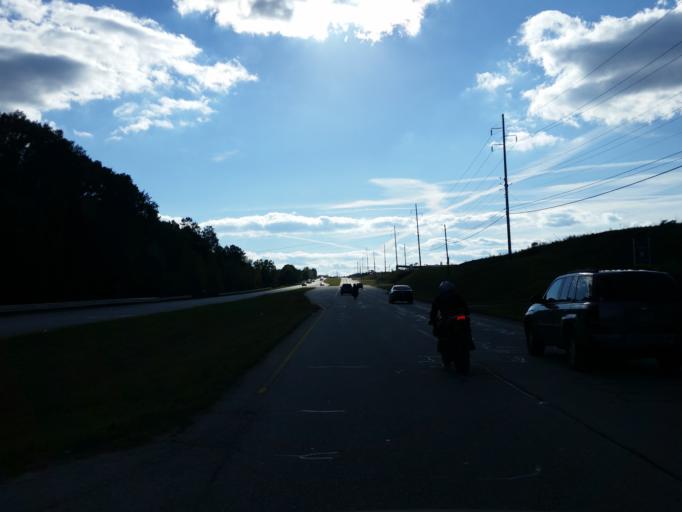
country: US
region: Georgia
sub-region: Paulding County
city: Hiram
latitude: 33.9214
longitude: -84.7598
